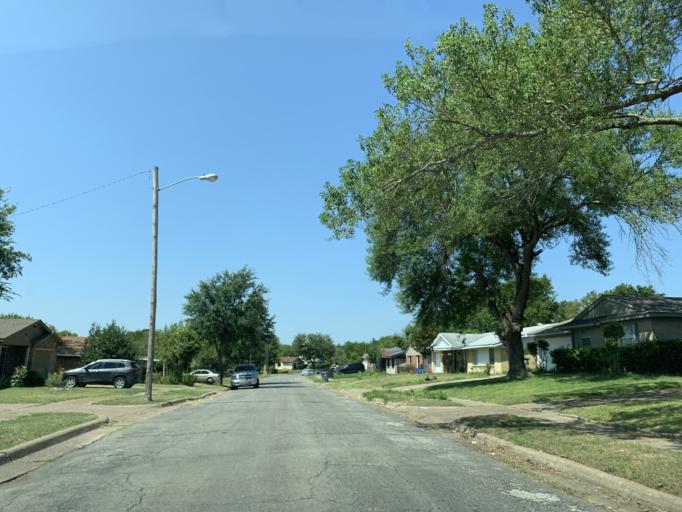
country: US
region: Texas
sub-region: Dallas County
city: Hutchins
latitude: 32.6725
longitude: -96.7524
